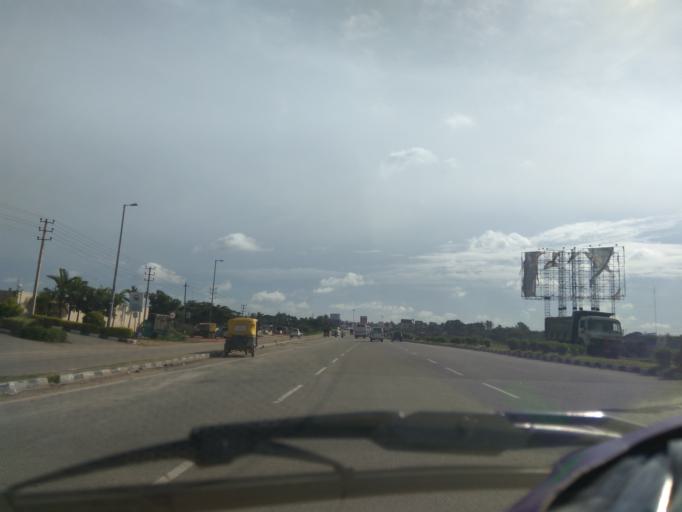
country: IN
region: Karnataka
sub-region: Bangalore Rural
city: Hoskote
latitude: 13.0612
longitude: 77.7722
